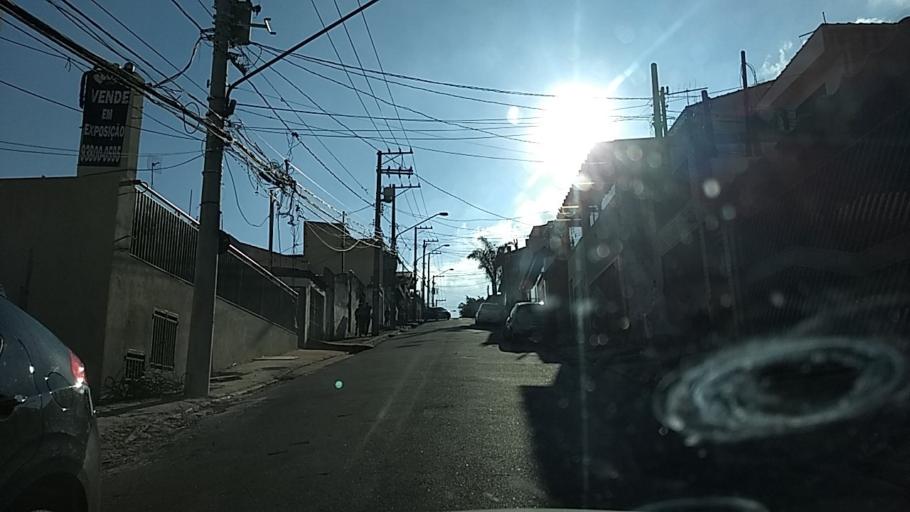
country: BR
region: Sao Paulo
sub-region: Guarulhos
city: Guarulhos
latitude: -23.4847
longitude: -46.5936
